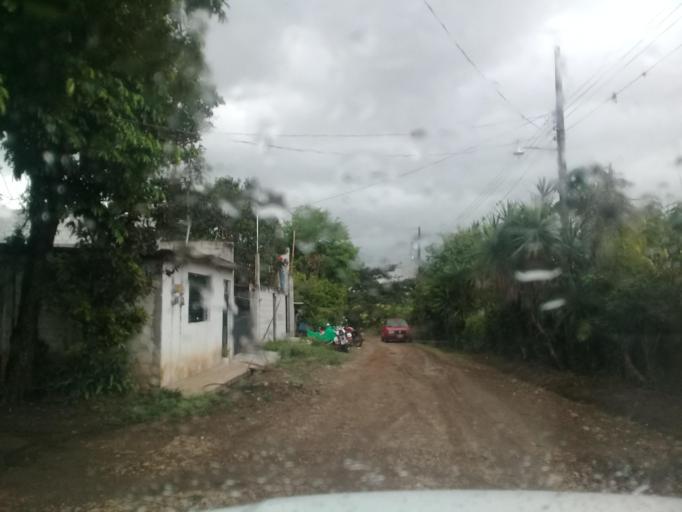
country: MX
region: Veracruz
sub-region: Amatlan de los Reyes
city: Trapiche Viejo
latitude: 18.8425
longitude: -96.9439
